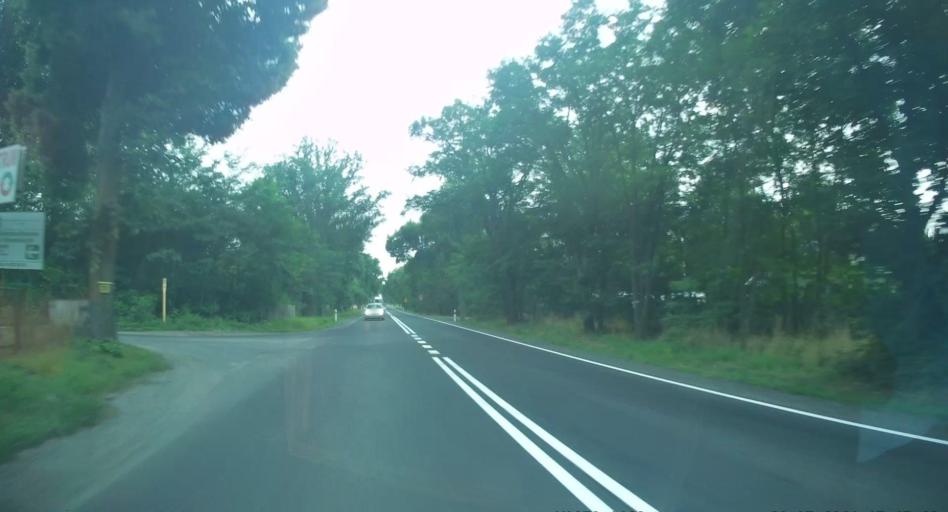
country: PL
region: Lodz Voivodeship
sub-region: Powiat radomszczanski
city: Gomunice
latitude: 51.1310
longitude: 19.4787
